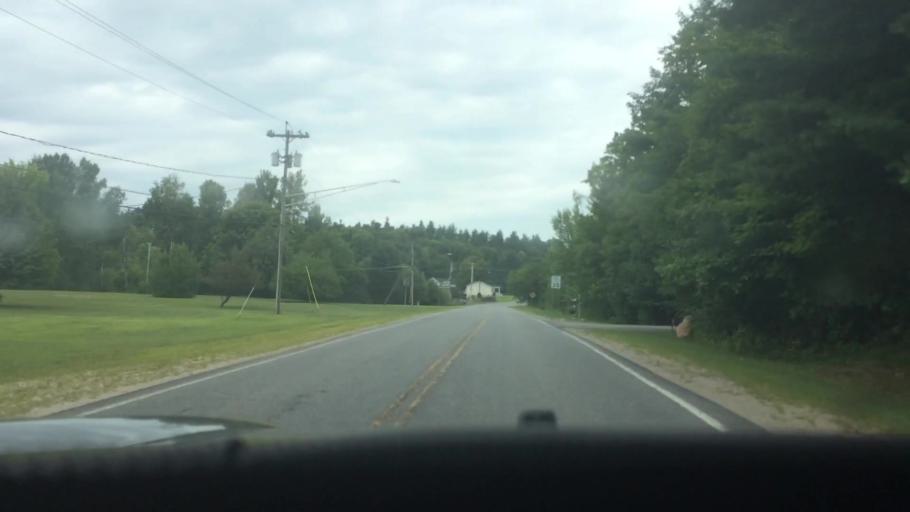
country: US
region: New York
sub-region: St. Lawrence County
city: Hannawa Falls
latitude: 44.5509
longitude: -74.9301
